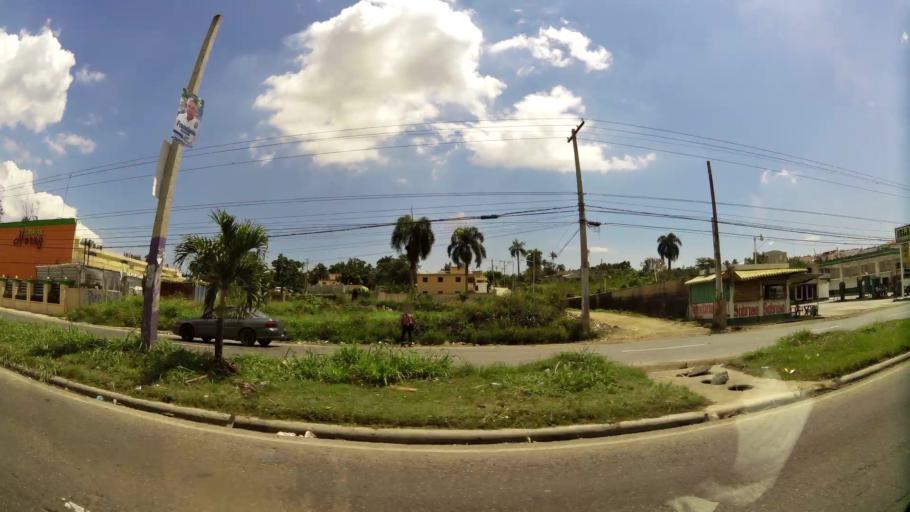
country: DO
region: Nacional
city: Ensanche Luperon
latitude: 18.5473
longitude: -69.8910
